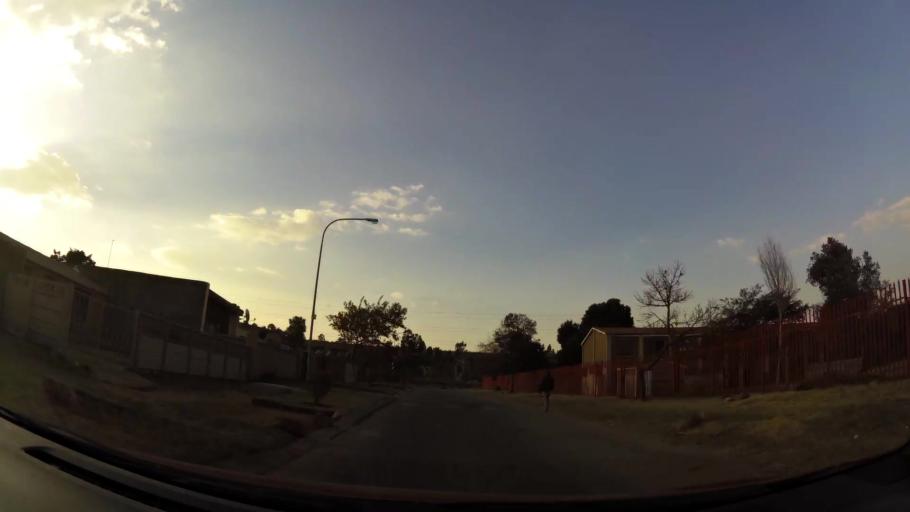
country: ZA
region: Gauteng
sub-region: City of Johannesburg Metropolitan Municipality
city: Roodepoort
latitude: -26.2083
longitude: 27.8959
